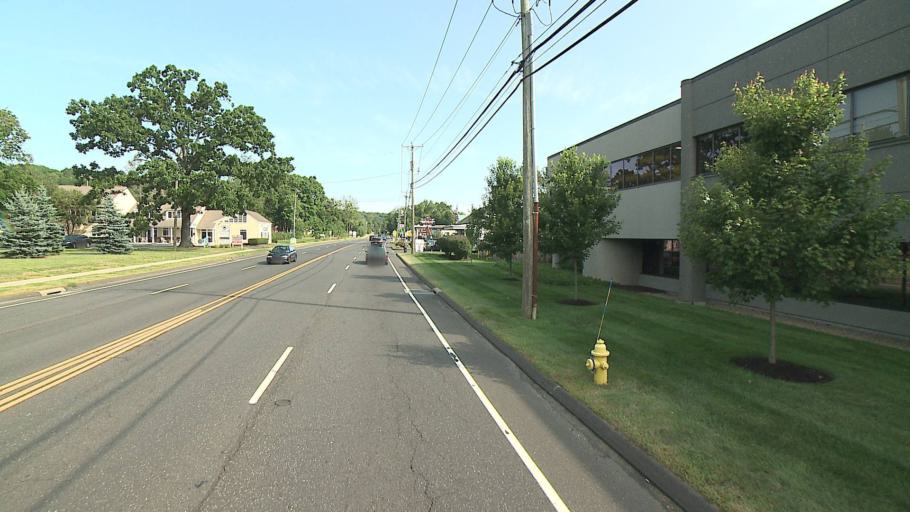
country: US
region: Connecticut
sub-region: Fairfield County
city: Wilton
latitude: 41.2075
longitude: -73.4308
